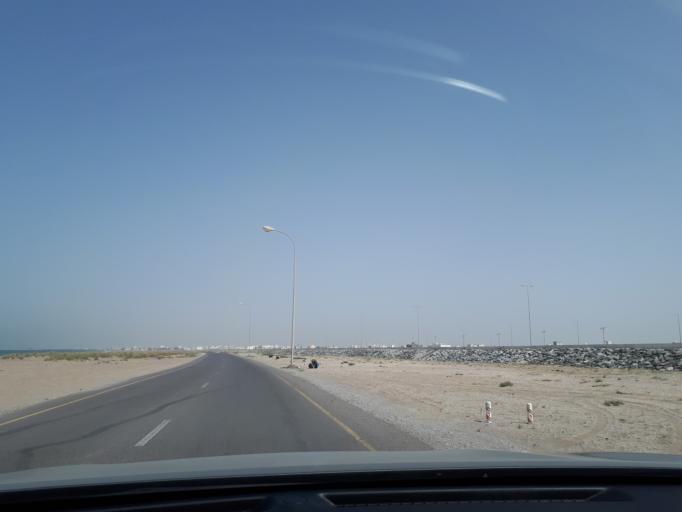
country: OM
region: Al Batinah
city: Barka'
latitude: 23.7183
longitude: 57.8598
